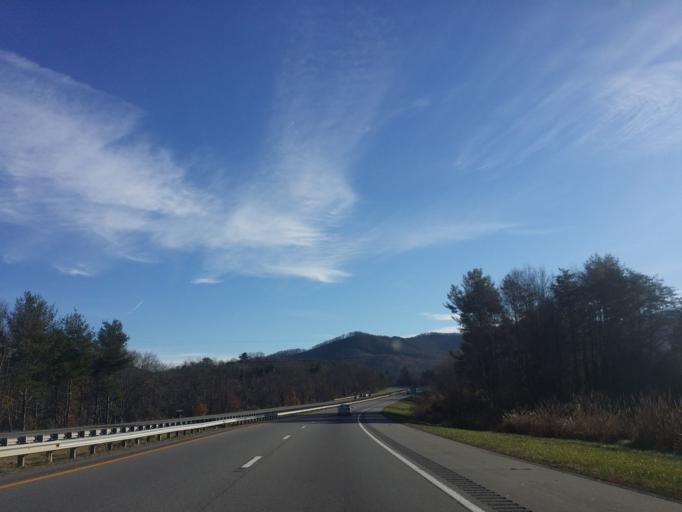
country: US
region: North Carolina
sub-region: Buncombe County
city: Black Mountain
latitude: 35.6068
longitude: -82.3381
